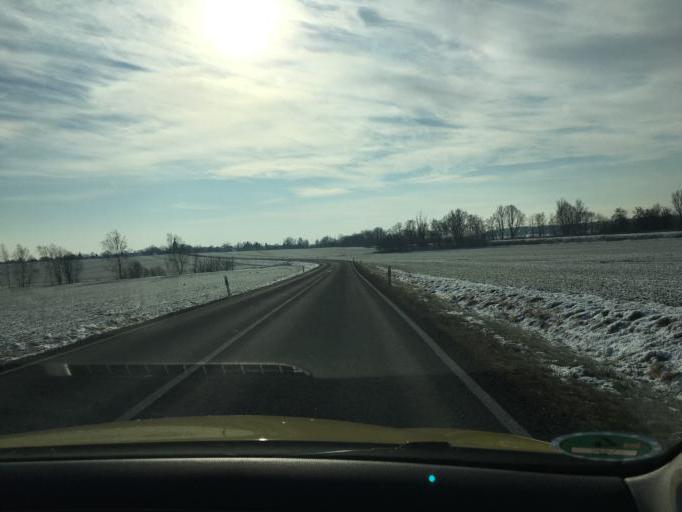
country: DE
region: Saxony
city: Otterwisch
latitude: 51.1827
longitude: 12.6161
